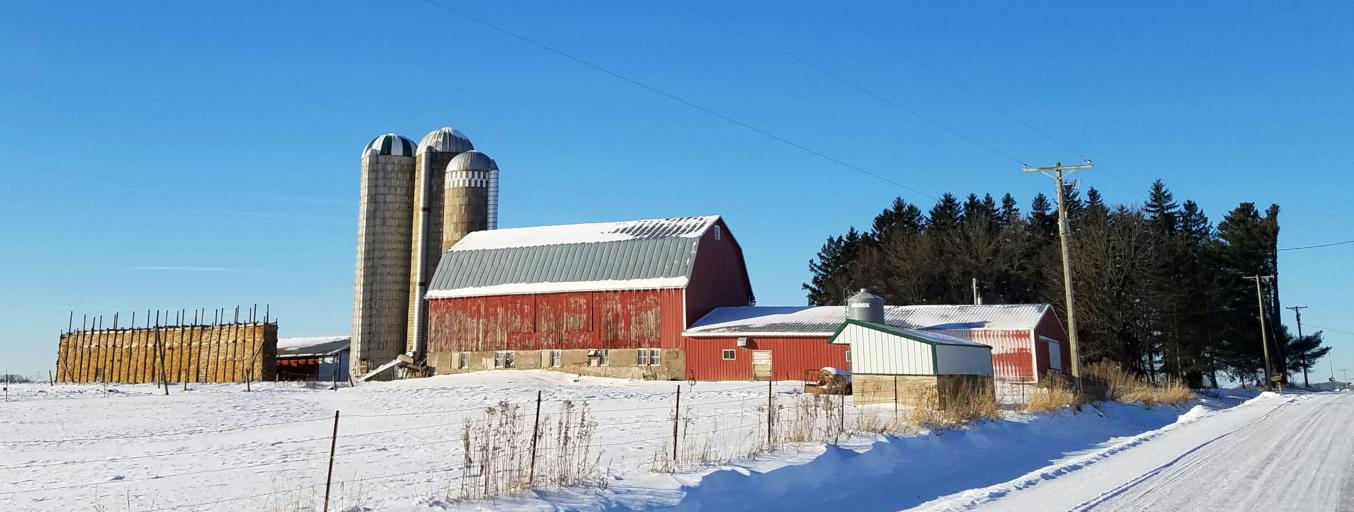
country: US
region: Wisconsin
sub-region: Clark County
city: Loyal
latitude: 44.6260
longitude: -90.3890
